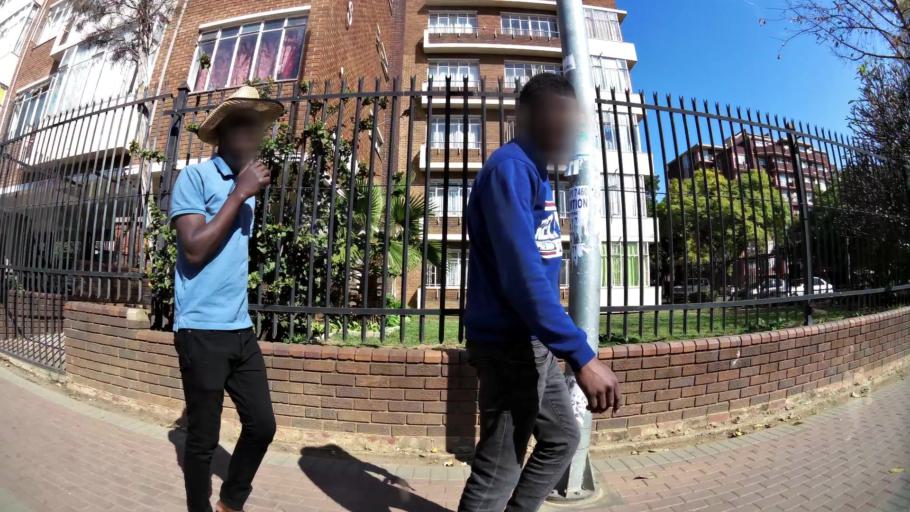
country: ZA
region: Gauteng
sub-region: City of Tshwane Metropolitan Municipality
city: Pretoria
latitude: -25.7545
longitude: 28.2059
